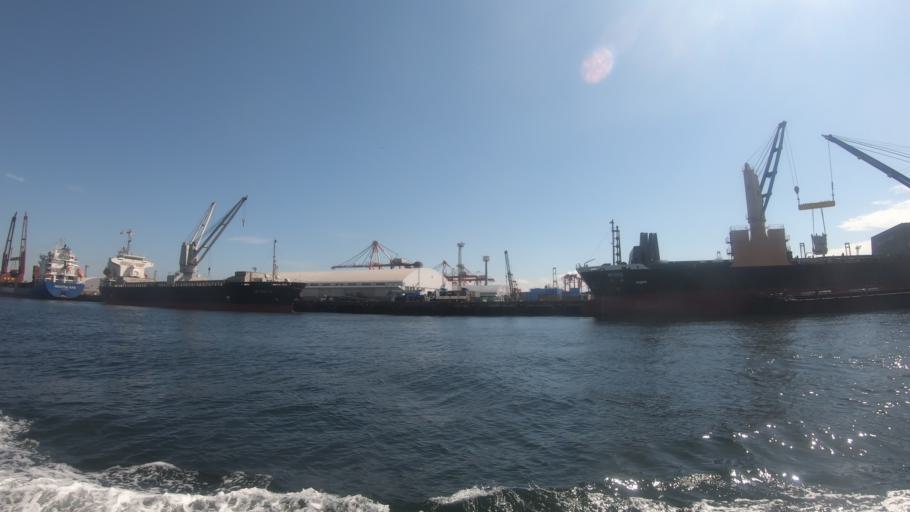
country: JP
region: Kanagawa
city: Yokohama
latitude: 35.4425
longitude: 139.6719
